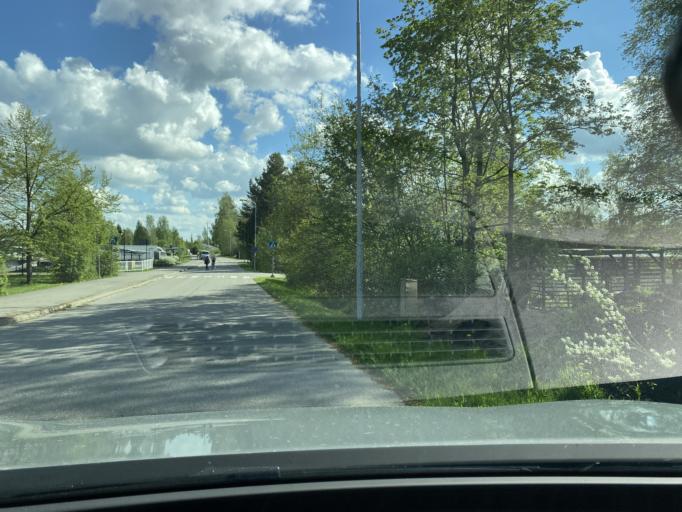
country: FI
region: Uusimaa
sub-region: Helsinki
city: Maentsaelae
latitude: 60.6478
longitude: 25.3171
